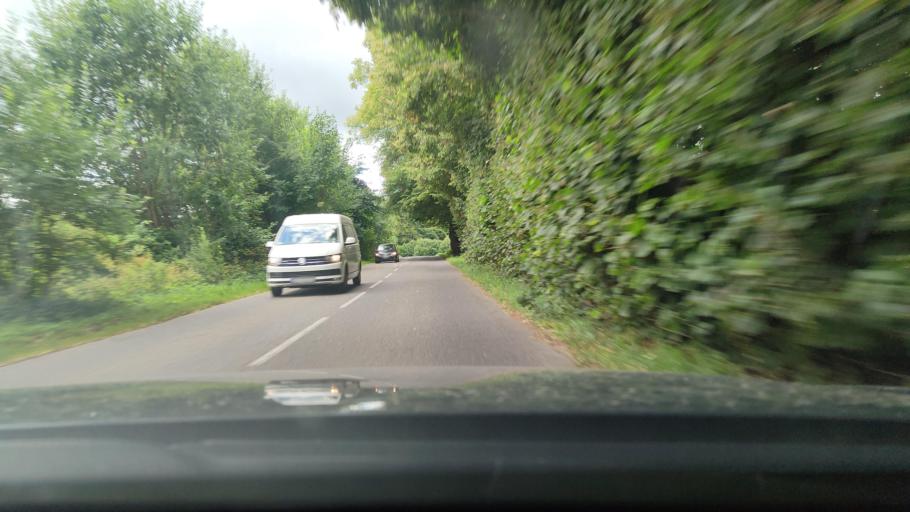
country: PL
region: Pomeranian Voivodeship
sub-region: Powiat pucki
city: Krokowa
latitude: 54.7375
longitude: 18.1597
